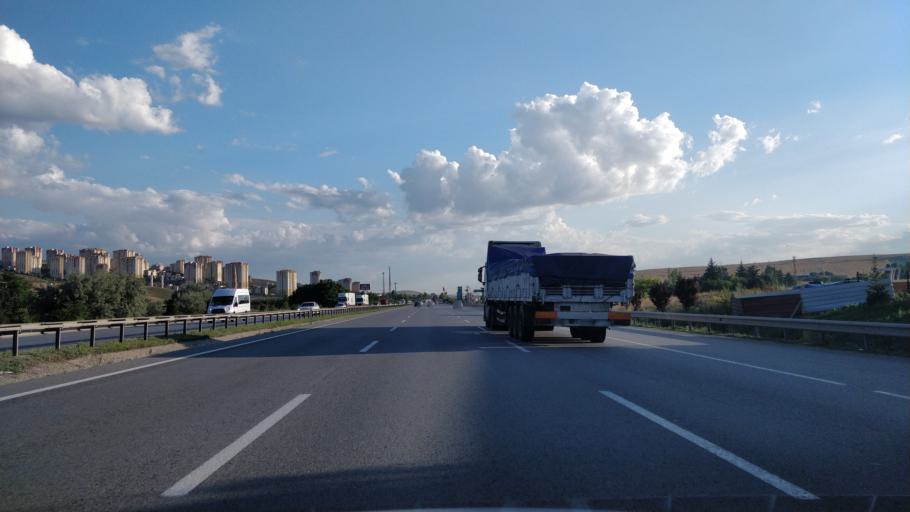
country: TR
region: Ankara
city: Etimesgut
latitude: 39.8287
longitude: 32.5781
